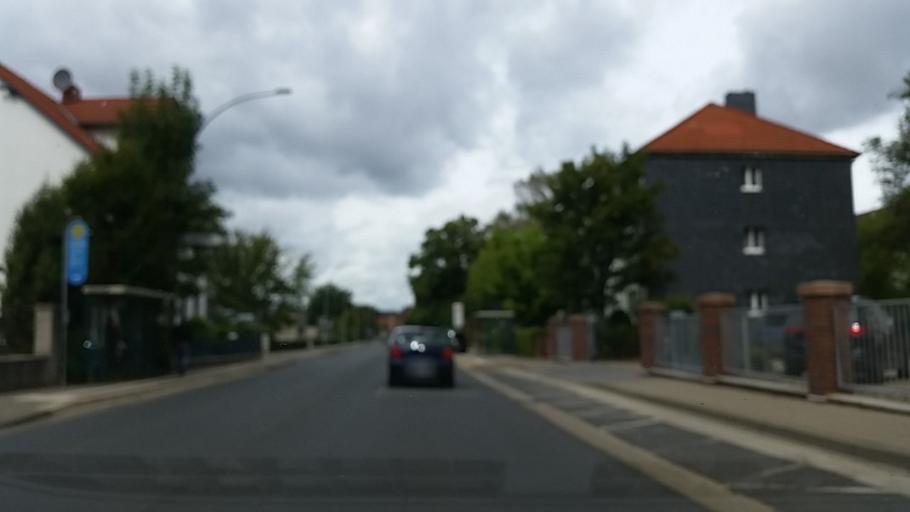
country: DE
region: Lower Saxony
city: Wolfenbuettel
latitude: 52.1589
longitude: 10.5495
